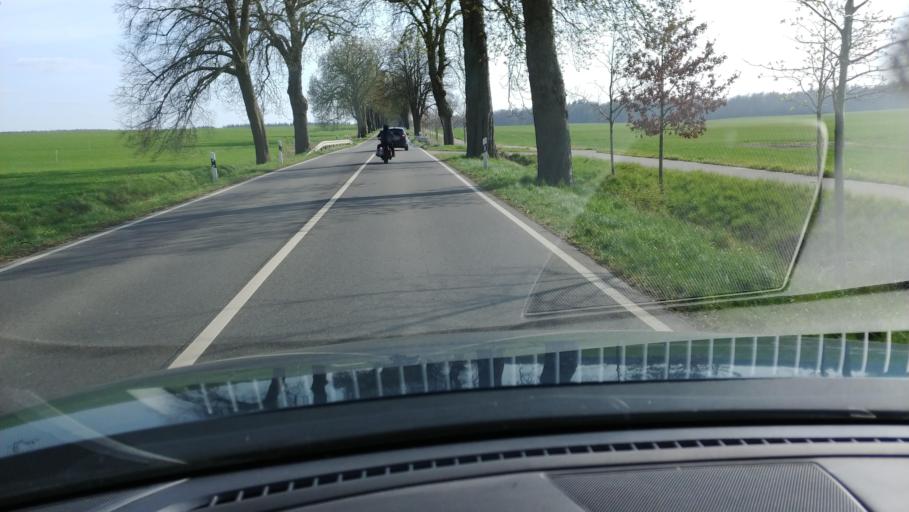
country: DE
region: Mecklenburg-Vorpommern
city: Lubstorf
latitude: 53.7512
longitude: 11.4120
